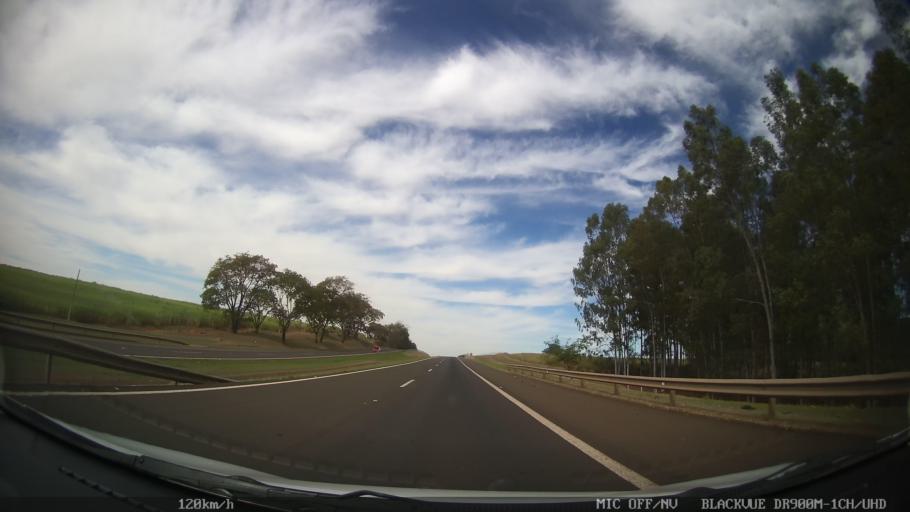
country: BR
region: Sao Paulo
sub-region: Matao
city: Matao
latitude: -21.5800
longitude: -48.4530
